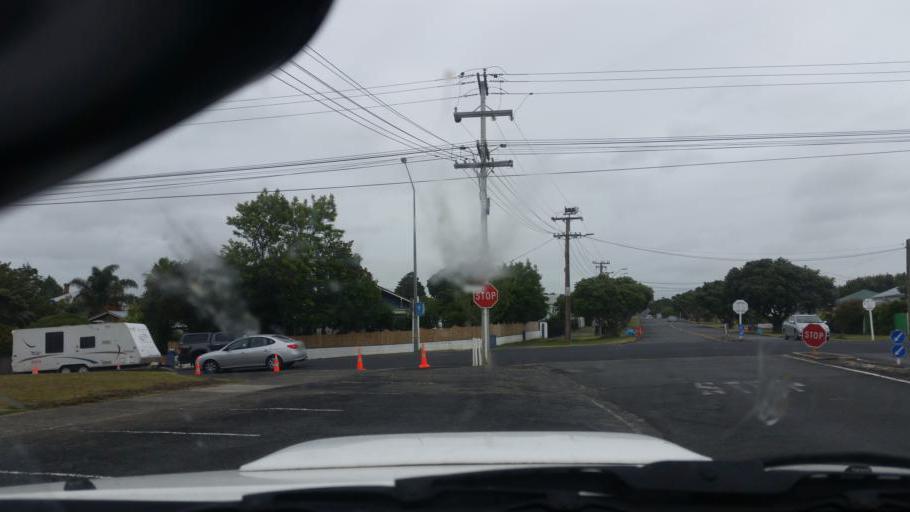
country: NZ
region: Northland
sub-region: Kaipara District
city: Dargaville
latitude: -35.9371
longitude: 173.8743
